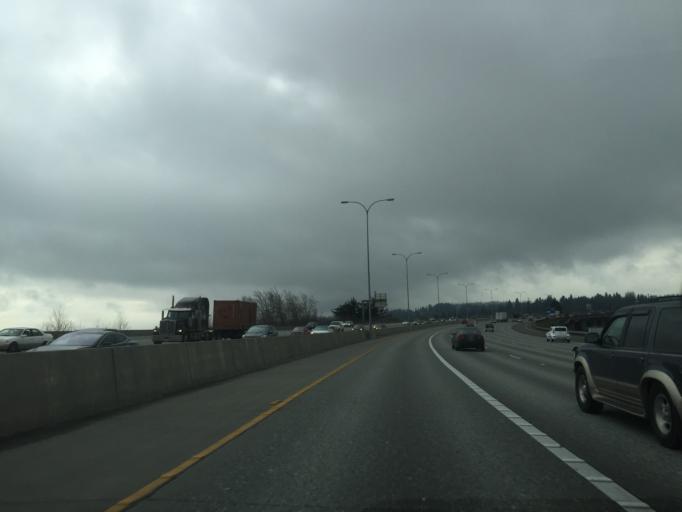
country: US
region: Washington
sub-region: Snohomish County
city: Everett
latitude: 47.9744
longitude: -122.1912
